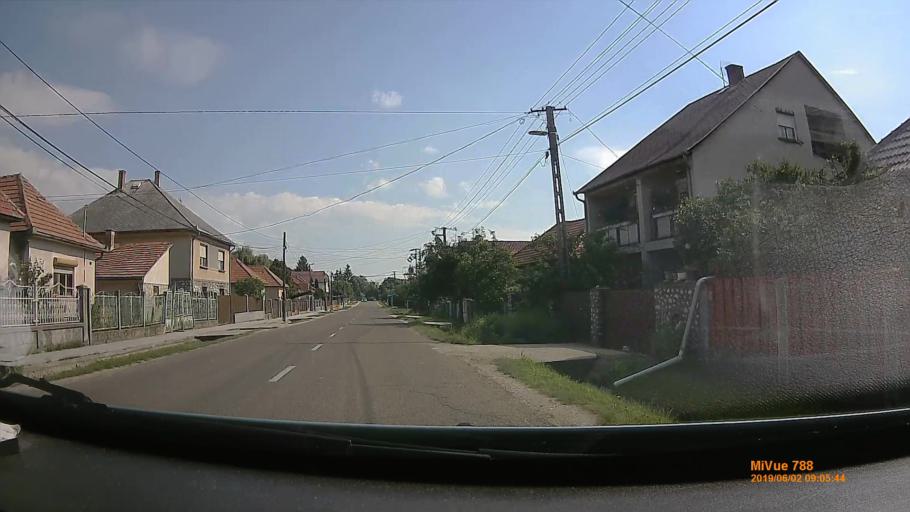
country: HU
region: Borsod-Abauj-Zemplen
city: Kazincbarcika
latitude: 48.1797
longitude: 20.6507
